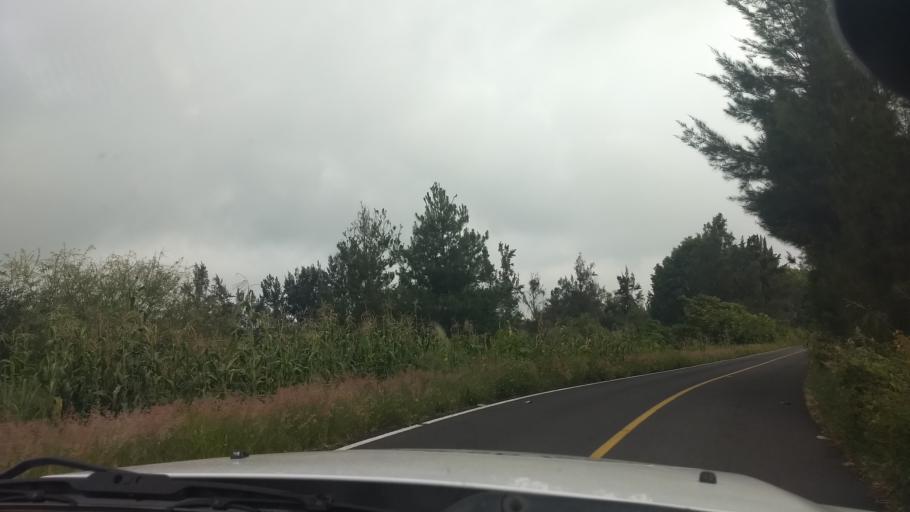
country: MX
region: Colima
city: Queseria
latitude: 19.4000
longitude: -103.6154
